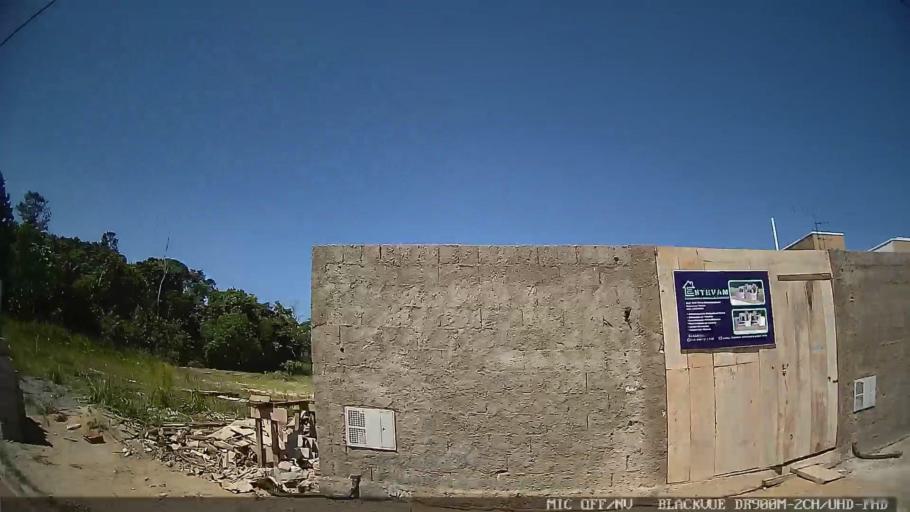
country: BR
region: Sao Paulo
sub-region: Peruibe
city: Peruibe
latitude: -24.2981
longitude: -46.9992
